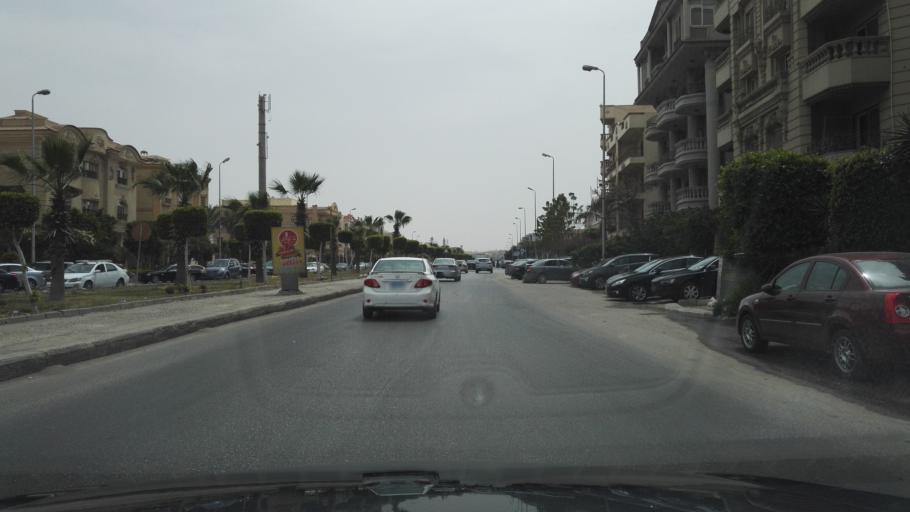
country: EG
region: Muhafazat al Qahirah
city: Cairo
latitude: 30.0071
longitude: 31.4125
